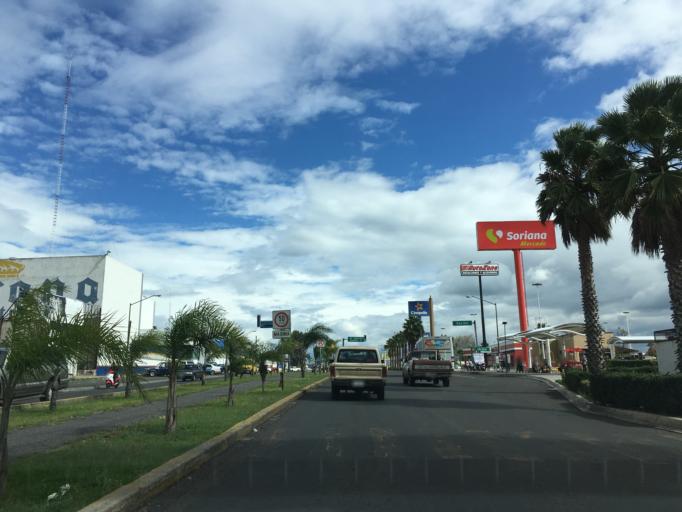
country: MX
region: Guanajuato
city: Moroleon
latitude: 20.1212
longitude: -101.1778
